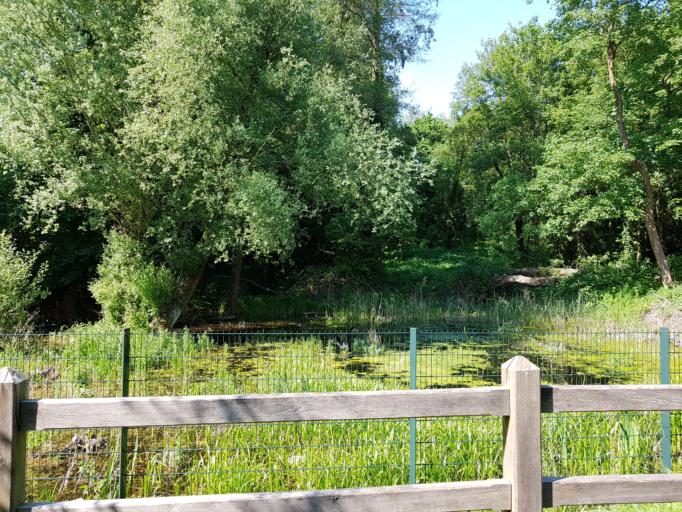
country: FR
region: Ile-de-France
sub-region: Departement des Hauts-de-Seine
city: Chatenay-Malabry
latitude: 48.7730
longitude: 2.2734
